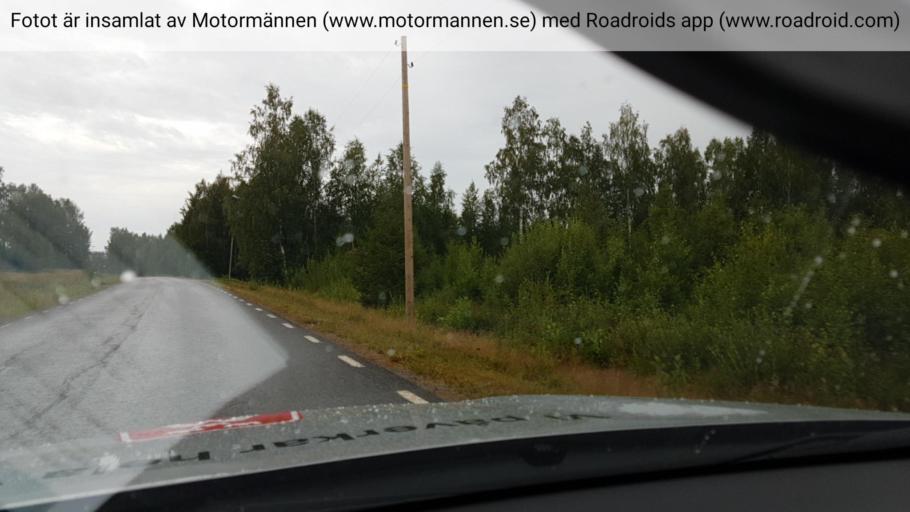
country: SE
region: Norrbotten
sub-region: Bodens Kommun
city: Boden
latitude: 65.8875
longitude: 21.3590
